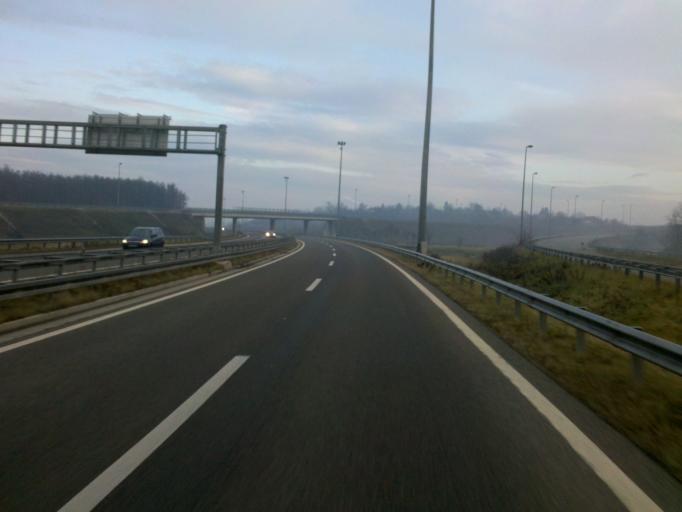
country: HR
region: Zagrebacka
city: Dubrava
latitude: 45.8944
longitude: 16.4984
